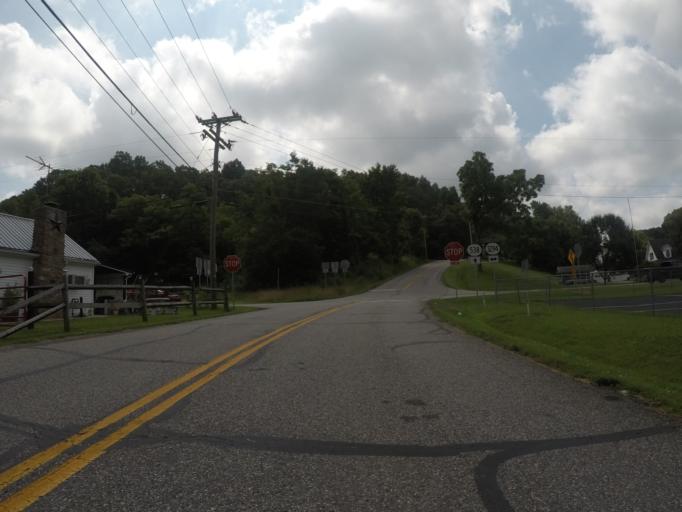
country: US
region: Kentucky
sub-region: Boyd County
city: Catlettsburg
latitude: 38.3996
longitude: -82.6550
